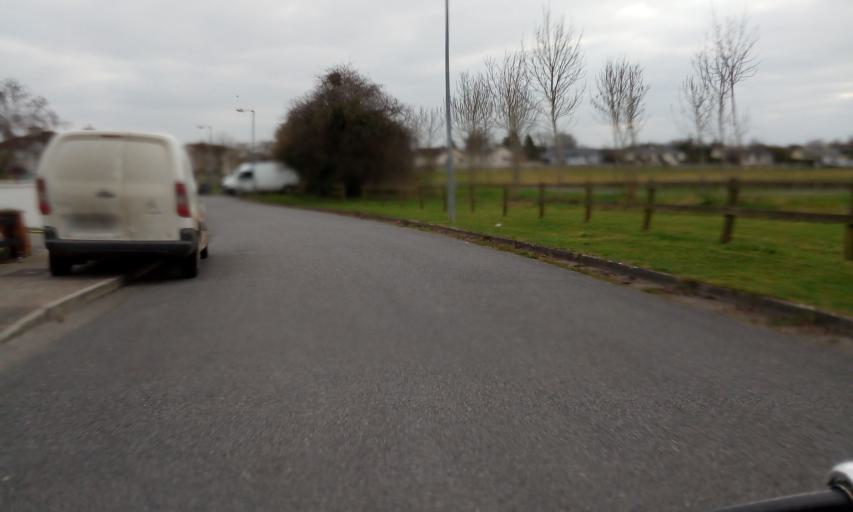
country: IE
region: Leinster
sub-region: Kilkenny
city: Kilkenny
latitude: 52.6649
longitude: -7.2322
